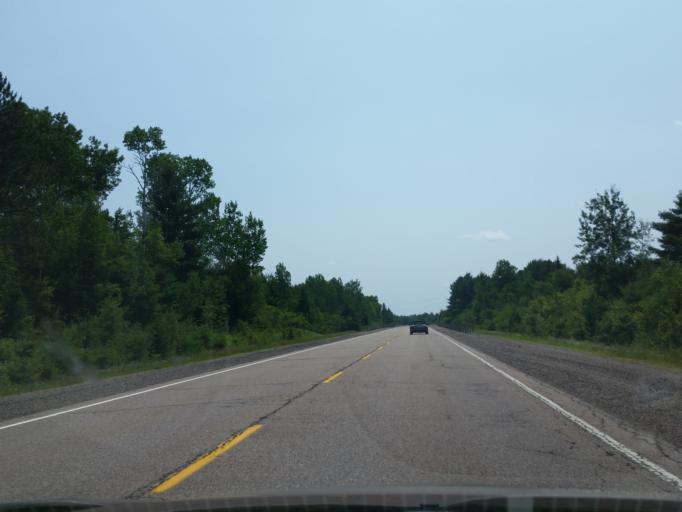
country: CA
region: Ontario
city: Petawawa
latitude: 45.8566
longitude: -77.2849
